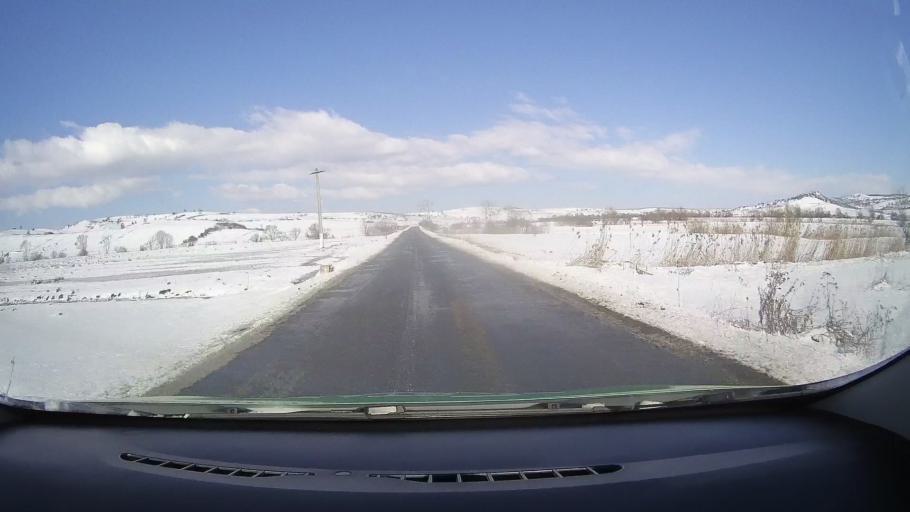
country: RO
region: Sibiu
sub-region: Comuna Vurpar
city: Vurpar
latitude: 45.8649
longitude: 24.3191
